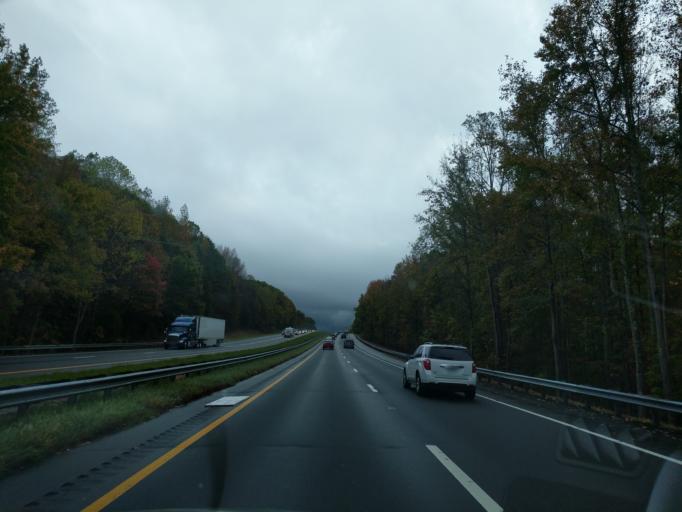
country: US
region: North Carolina
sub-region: Orange County
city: Hillsborough
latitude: 36.0489
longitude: -79.0532
